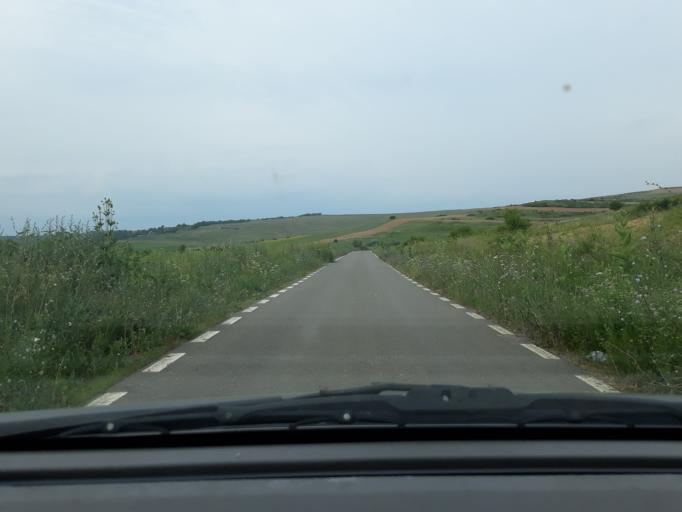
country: RO
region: Salaj
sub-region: Comuna Criseni
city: Criseni
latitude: 47.2743
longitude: 23.0763
